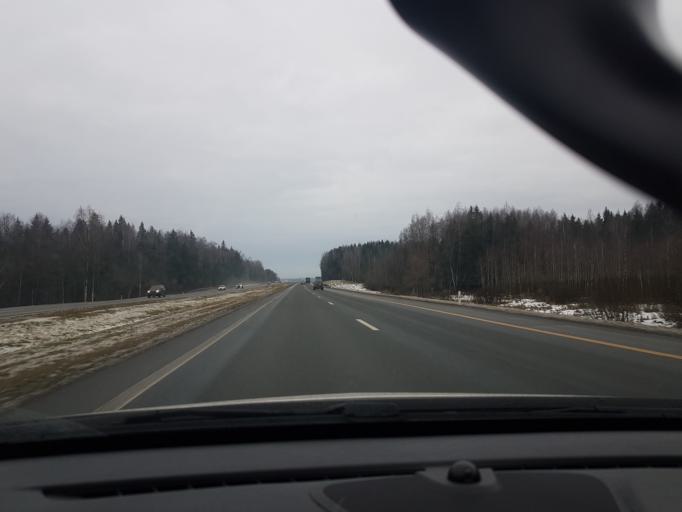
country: RU
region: Moskovskaya
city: Sychevo
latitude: 55.9873
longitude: 36.2934
